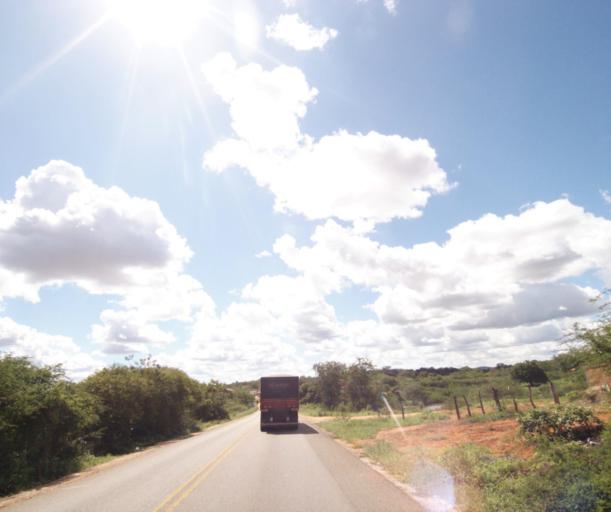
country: BR
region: Bahia
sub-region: Caetite
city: Caetite
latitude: -14.1703
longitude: -42.2274
